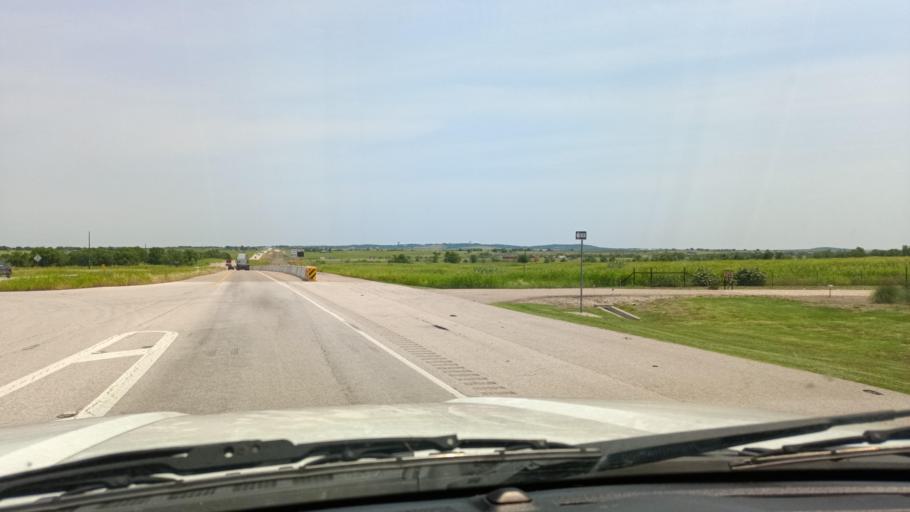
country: US
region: Texas
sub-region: Bell County
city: Little River-Academy
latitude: 30.9937
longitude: -97.2851
